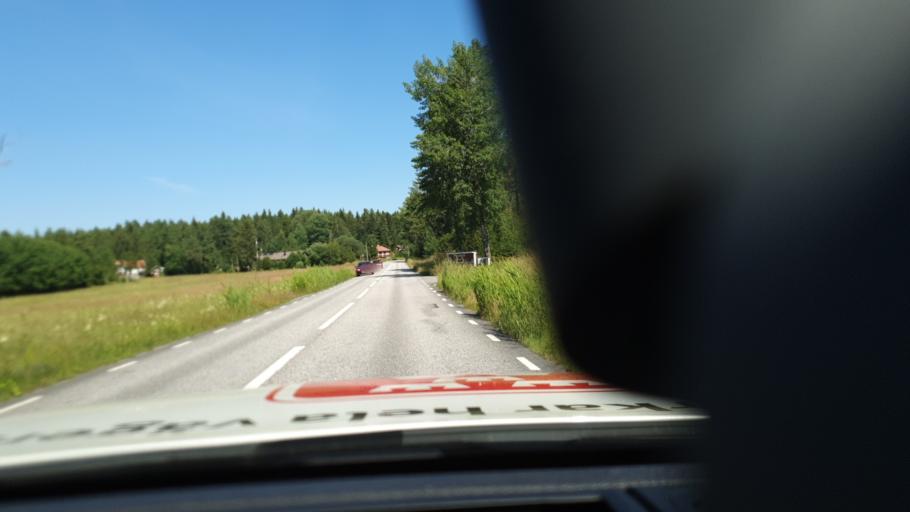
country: SE
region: Stockholm
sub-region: Norrtalje Kommun
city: Bjorko
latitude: 59.7935
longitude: 18.8683
